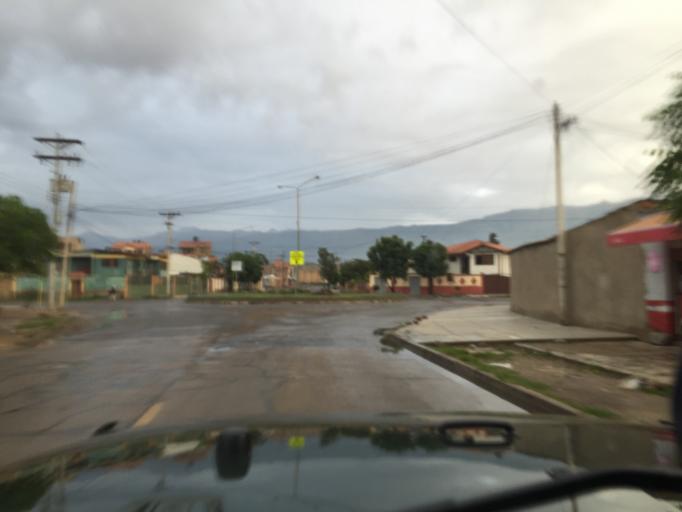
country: BO
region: Cochabamba
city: Cochabamba
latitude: -17.4171
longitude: -66.1680
